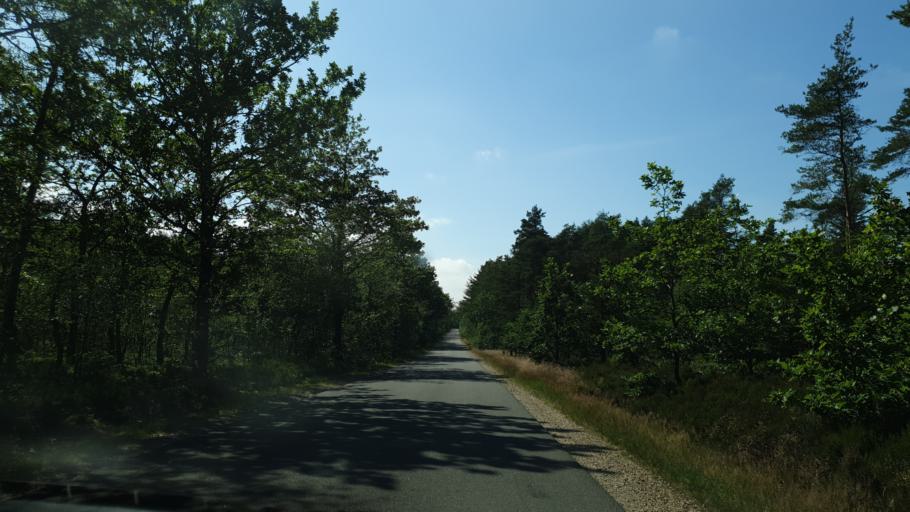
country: DK
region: Central Jutland
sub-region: Ringkobing-Skjern Kommune
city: Skjern
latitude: 55.9992
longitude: 8.4399
